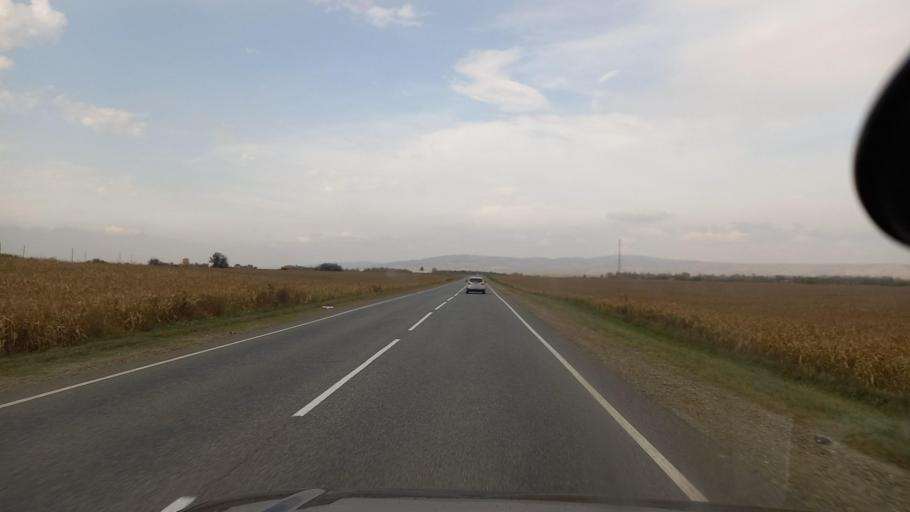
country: RU
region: Krasnodarskiy
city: Shedok
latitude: 44.2581
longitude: 40.8670
